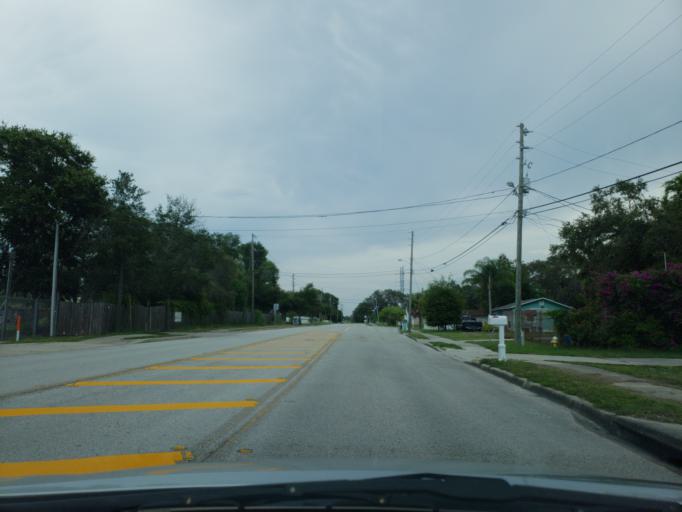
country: US
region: Florida
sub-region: Pinellas County
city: Tarpon Springs
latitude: 28.1542
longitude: -82.7478
